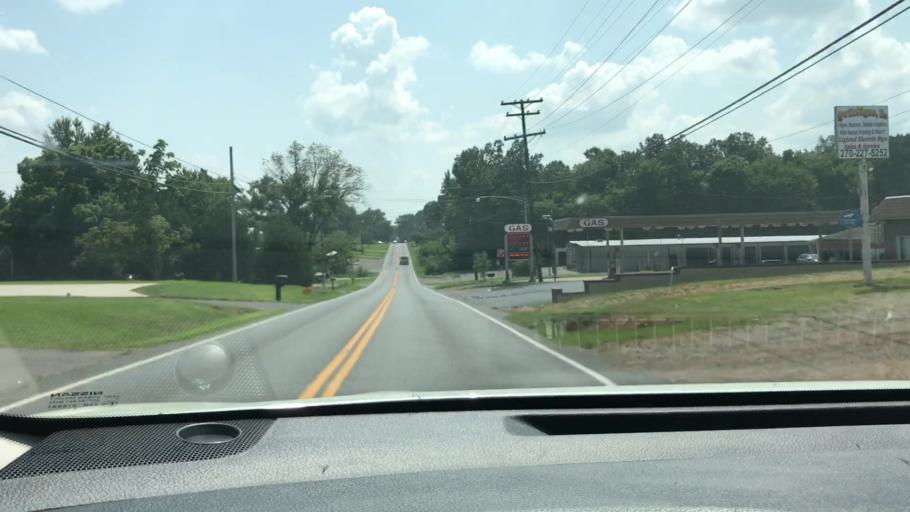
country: US
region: Kentucky
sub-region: Calloway County
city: Murray
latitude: 36.6005
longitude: -88.3031
